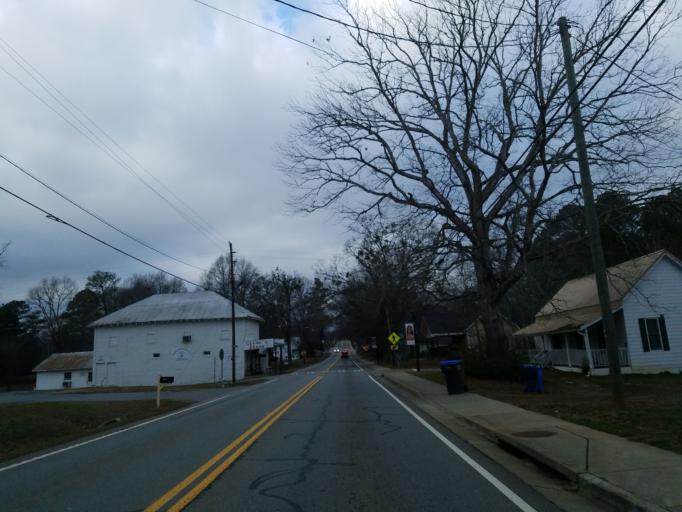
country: US
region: Georgia
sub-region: Cherokee County
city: Canton
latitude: 34.3152
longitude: -84.5507
